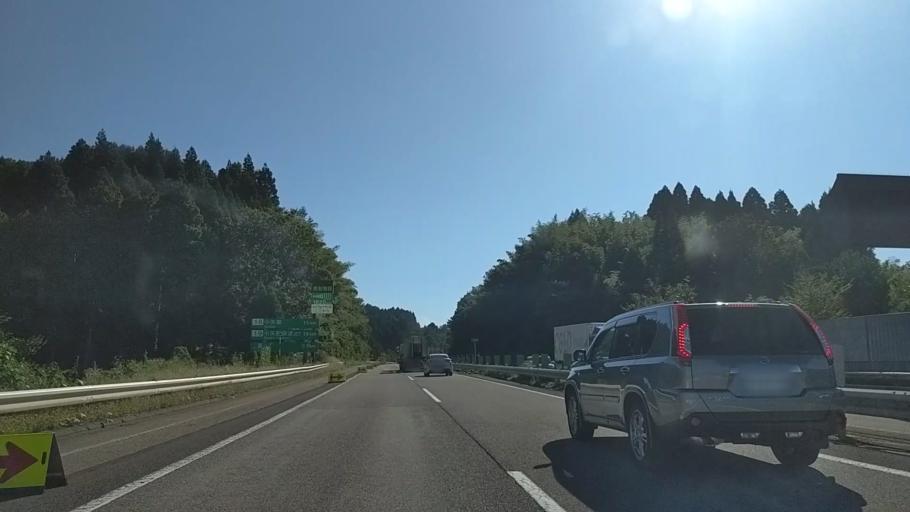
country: JP
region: Ishikawa
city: Tsubata
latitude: 36.6062
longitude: 136.7123
